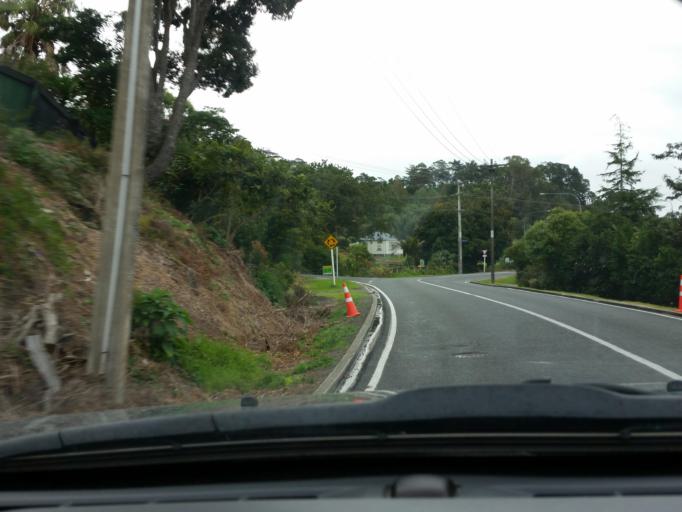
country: NZ
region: Northland
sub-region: Kaipara District
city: Dargaville
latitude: -35.9577
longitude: 173.8675
